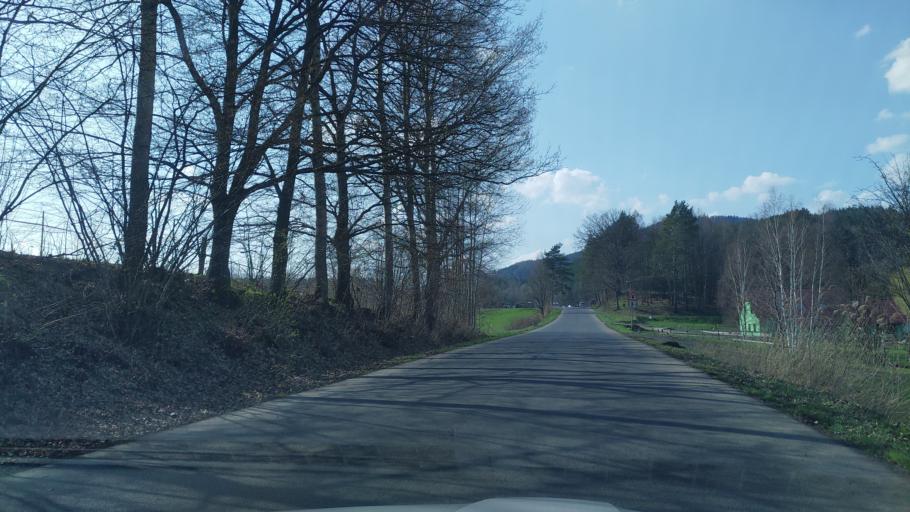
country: CZ
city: Cvikov
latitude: 50.7697
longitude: 14.6740
